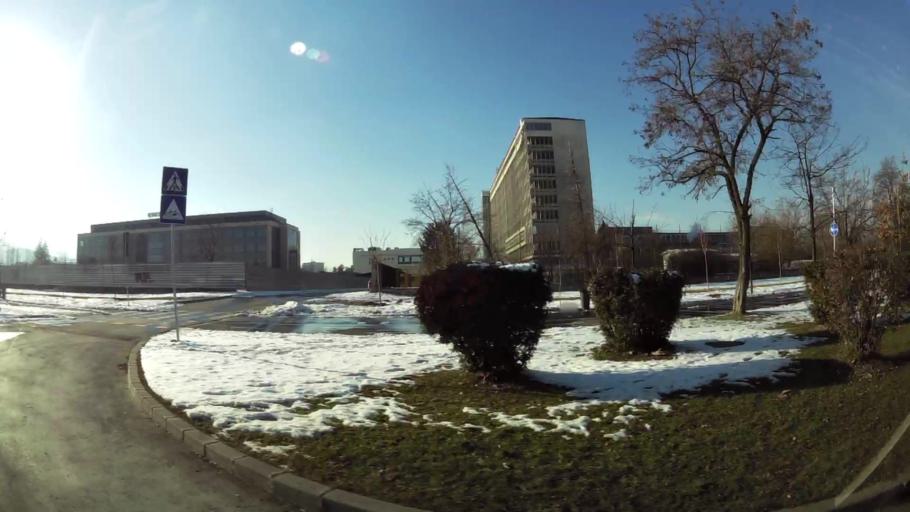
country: MK
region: Karpos
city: Skopje
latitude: 42.0047
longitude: 21.4052
